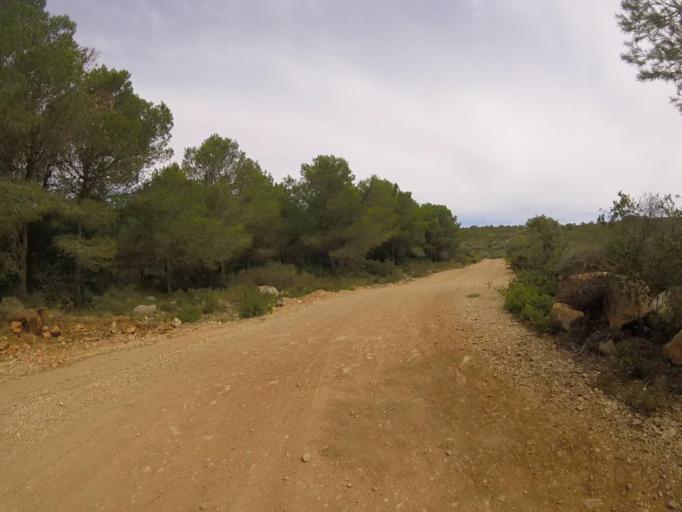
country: ES
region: Valencia
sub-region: Provincia de Castello
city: Cabanes
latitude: 40.1902
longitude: 0.0891
